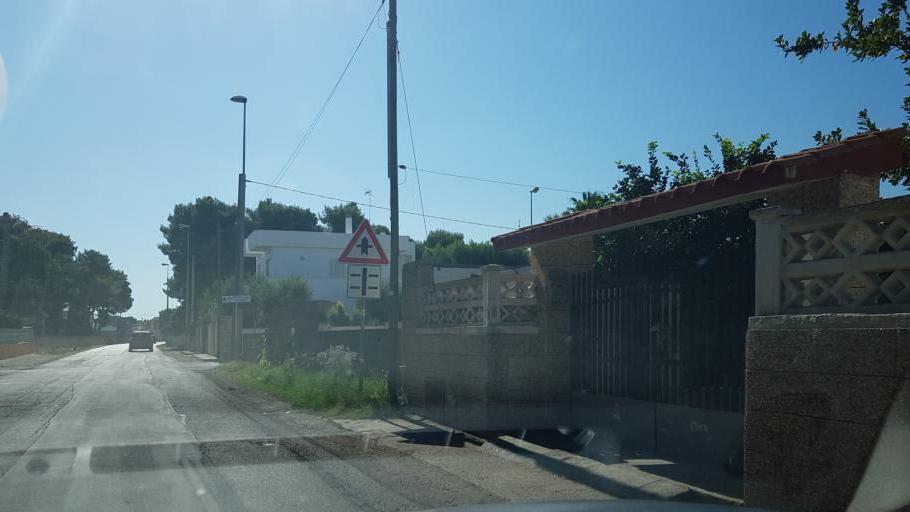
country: IT
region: Apulia
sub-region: Provincia di Lecce
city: Porto Cesareo
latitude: 40.2606
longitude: 17.9032
